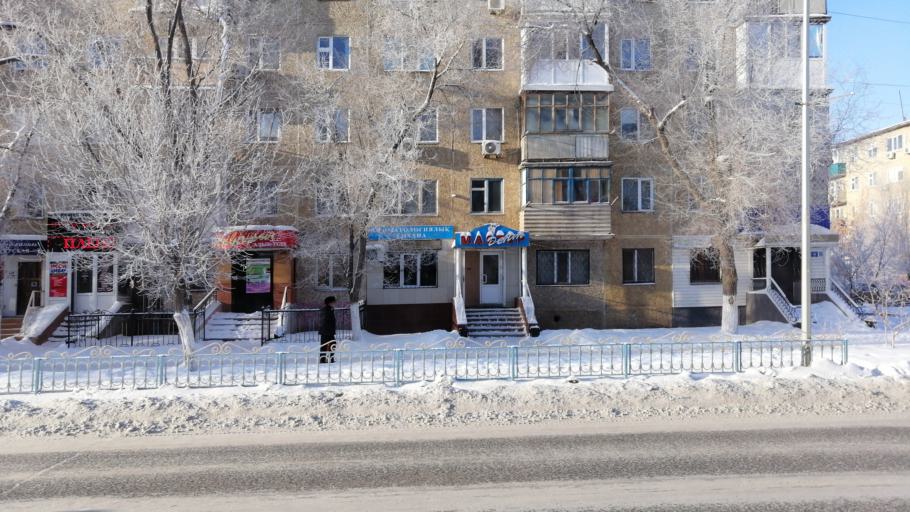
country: KZ
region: Aqtoebe
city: Aqtobe
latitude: 50.3038
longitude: 57.1521
